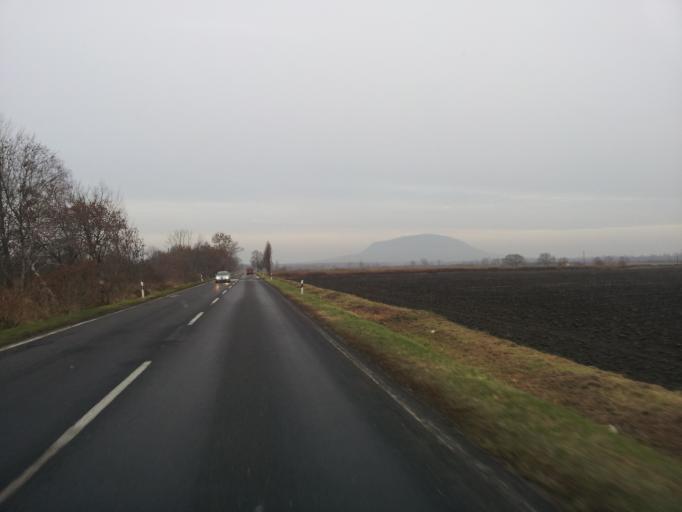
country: HU
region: Veszprem
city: Devecser
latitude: 47.1149
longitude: 17.4282
